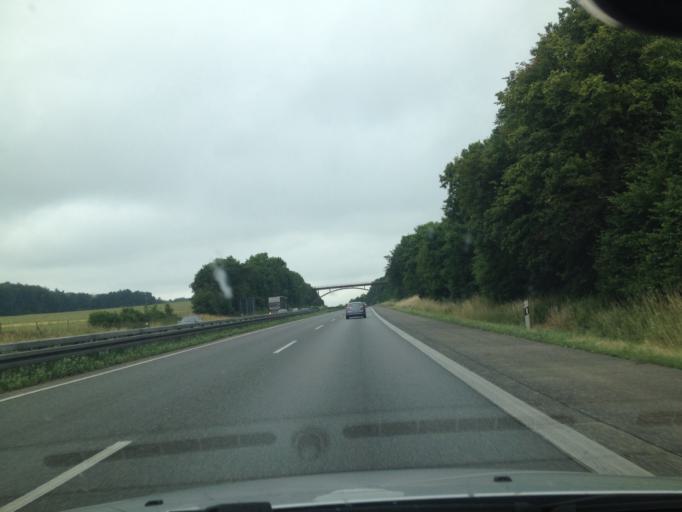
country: DE
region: Hesse
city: Allendorf an der Lahn
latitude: 50.5340
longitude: 8.5847
